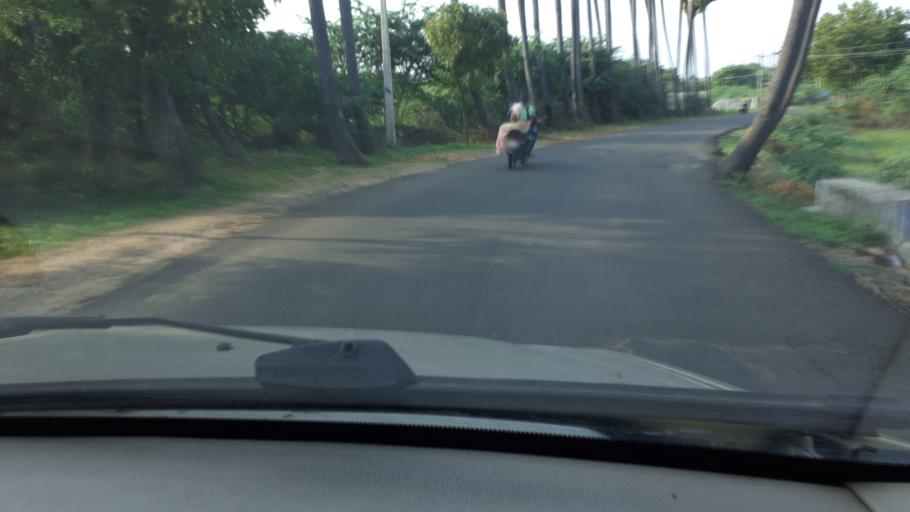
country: IN
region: Tamil Nadu
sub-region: Thoothukkudi
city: Alwar Tirunagari
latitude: 8.5890
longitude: 77.9786
